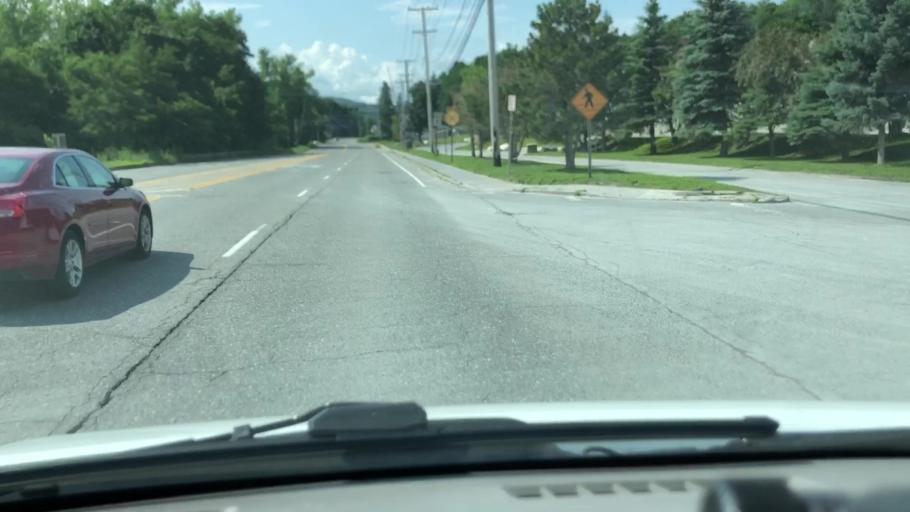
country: US
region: Massachusetts
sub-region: Berkshire County
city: Adams
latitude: 42.6432
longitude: -73.1123
